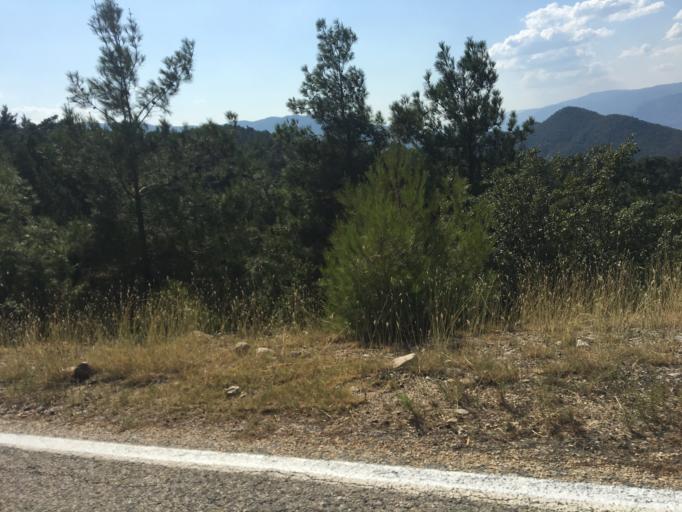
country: TR
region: Ankara
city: Beydili
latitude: 40.0633
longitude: 30.9208
